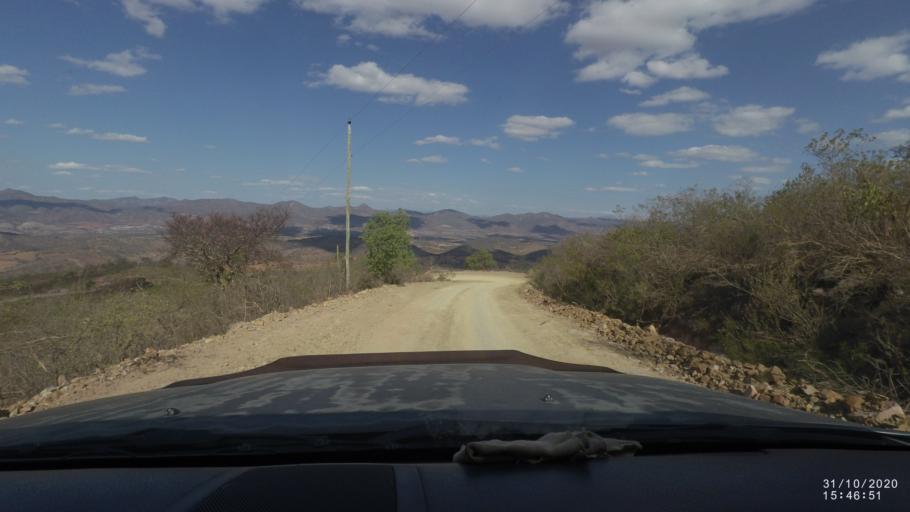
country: BO
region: Chuquisaca
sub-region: Provincia Zudanez
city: Mojocoya
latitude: -18.3149
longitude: -64.7161
